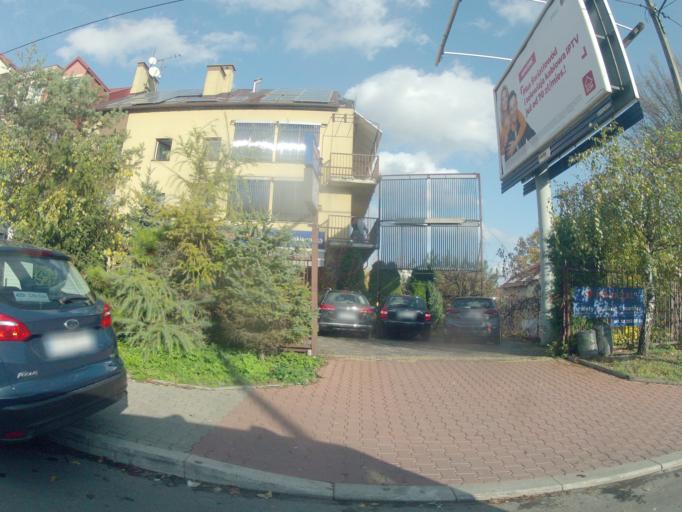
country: PL
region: Lesser Poland Voivodeship
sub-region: Krakow
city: Krakow
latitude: 50.0598
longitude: 19.8946
